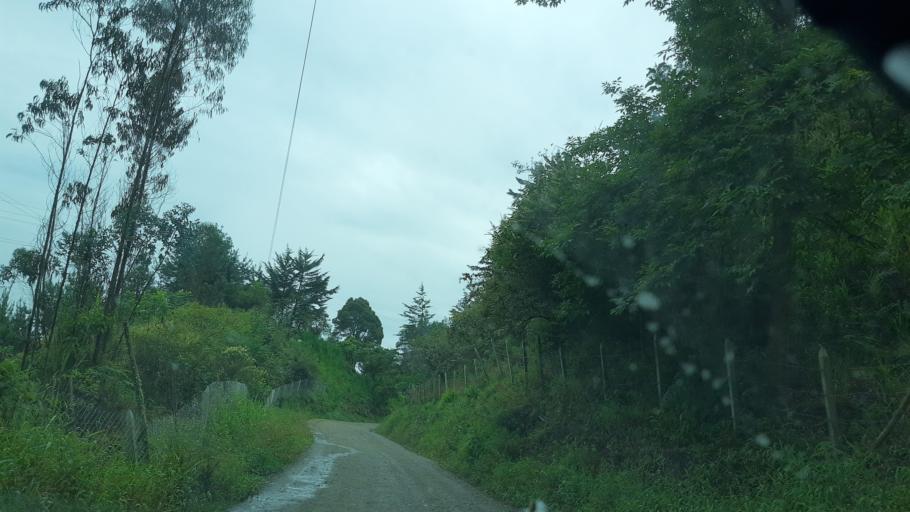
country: CO
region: Cundinamarca
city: Tenza
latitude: 5.0394
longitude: -73.4311
